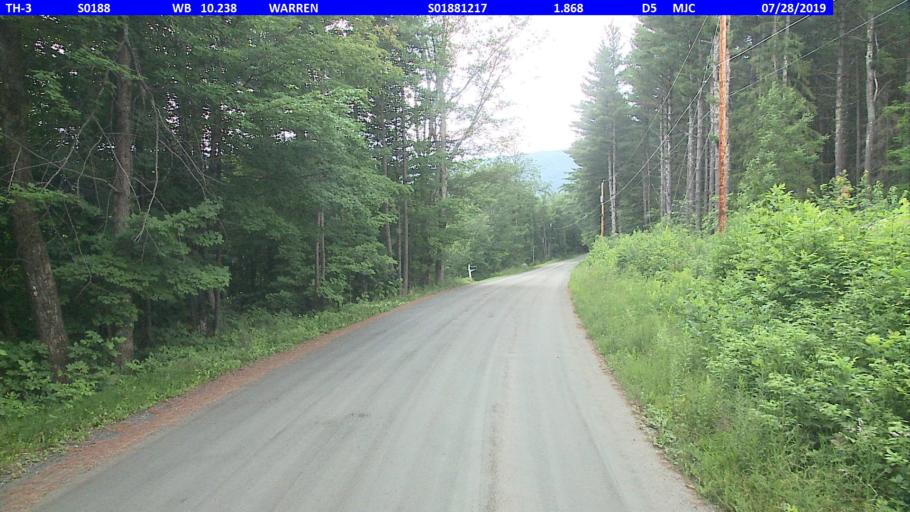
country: US
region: Vermont
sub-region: Addison County
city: Bristol
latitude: 44.1000
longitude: -72.8948
